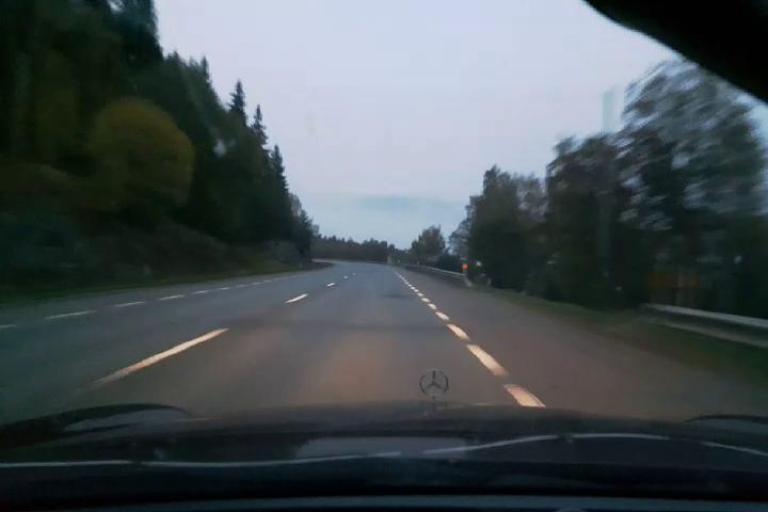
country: SE
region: Vaesternorrland
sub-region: Kramfors Kommun
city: Nordingra
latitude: 63.0061
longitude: 18.2651
